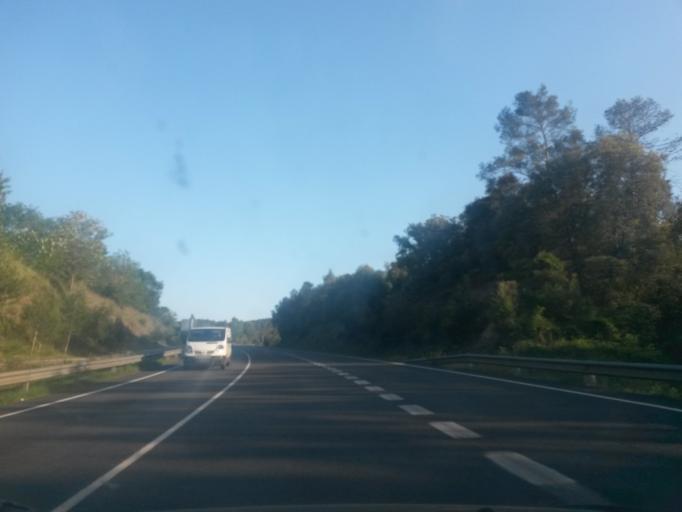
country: ES
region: Catalonia
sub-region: Provincia de Girona
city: Besalu
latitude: 42.1743
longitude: 2.7375
